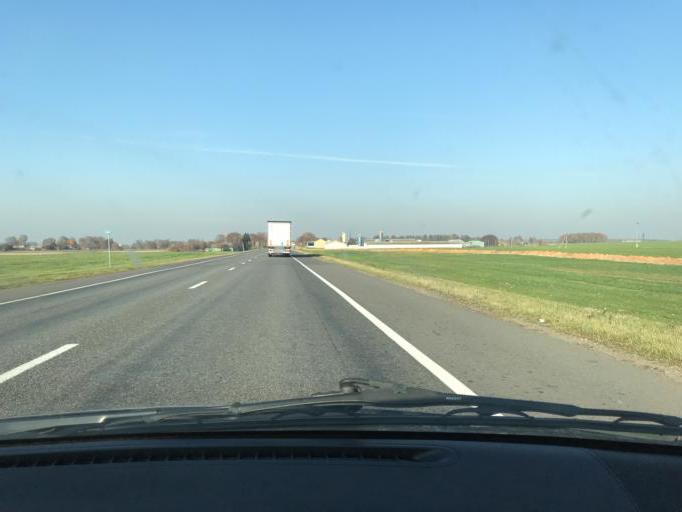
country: BY
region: Mogilev
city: Shklow
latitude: 54.2429
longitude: 30.4511
